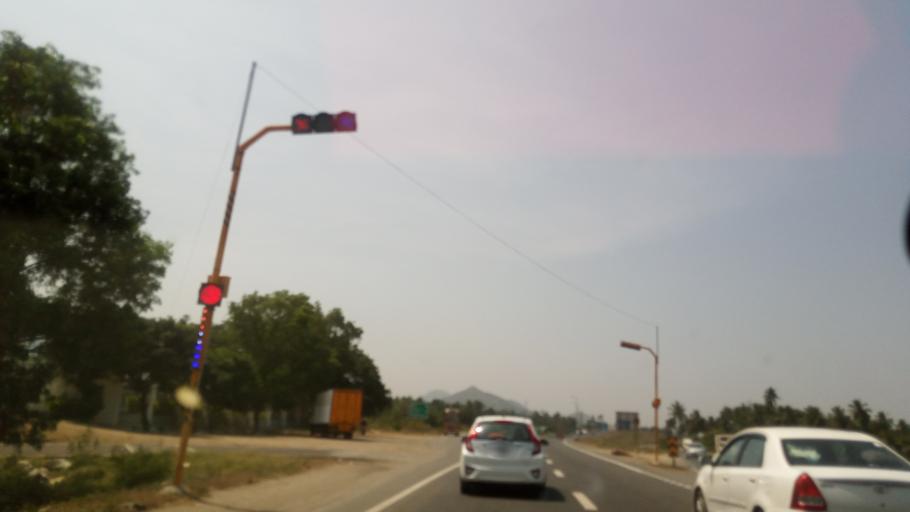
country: IN
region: Tamil Nadu
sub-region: Salem
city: Salem
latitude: 11.6649
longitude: 78.2497
